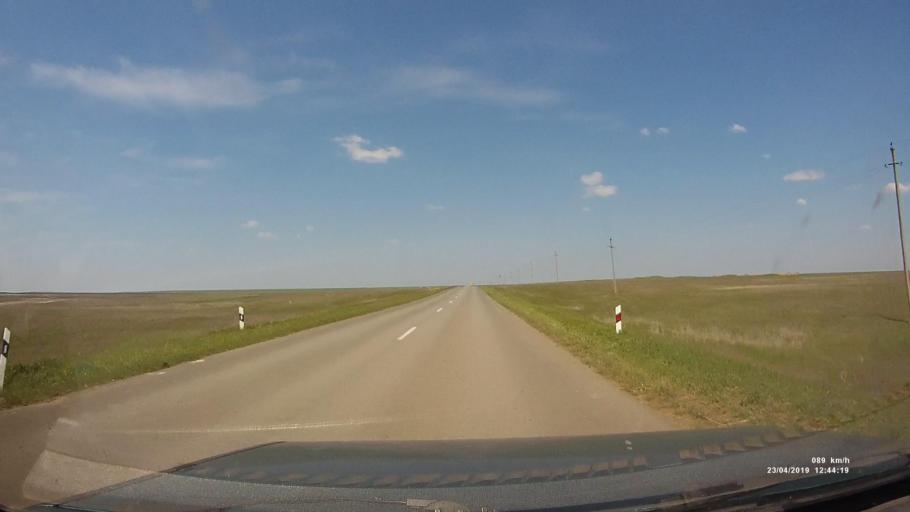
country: RU
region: Kalmykiya
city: Yashalta
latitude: 46.4754
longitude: 42.6480
